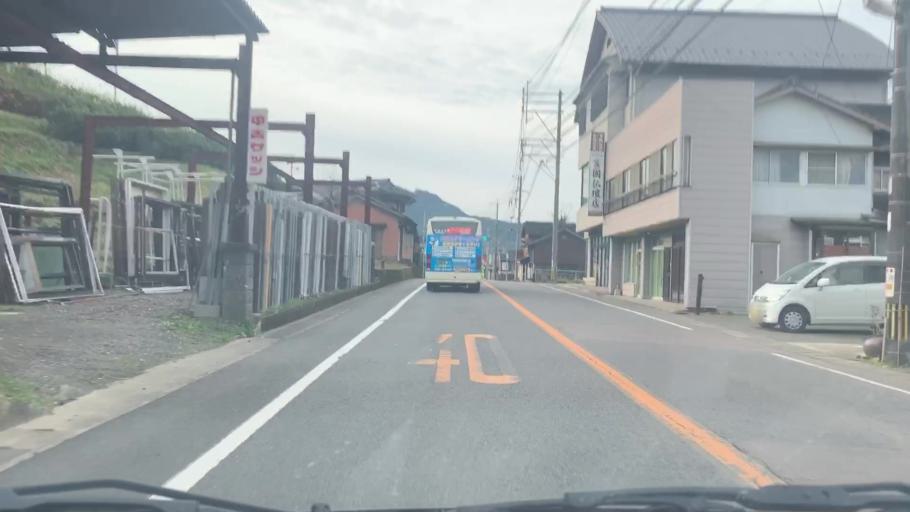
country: JP
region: Saga Prefecture
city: Ureshinomachi-shimojuku
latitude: 33.1128
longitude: 130.0010
